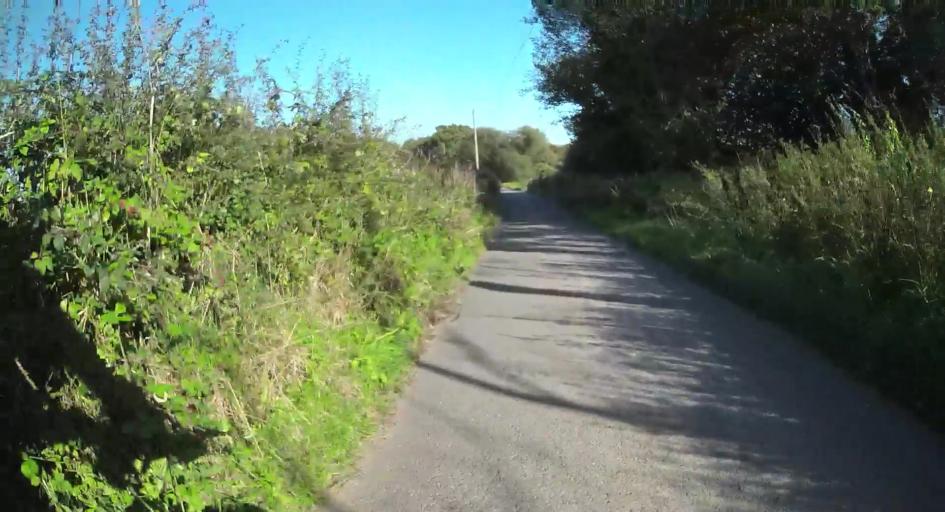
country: GB
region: England
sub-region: Isle of Wight
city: Chale
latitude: 50.6412
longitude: -1.3091
